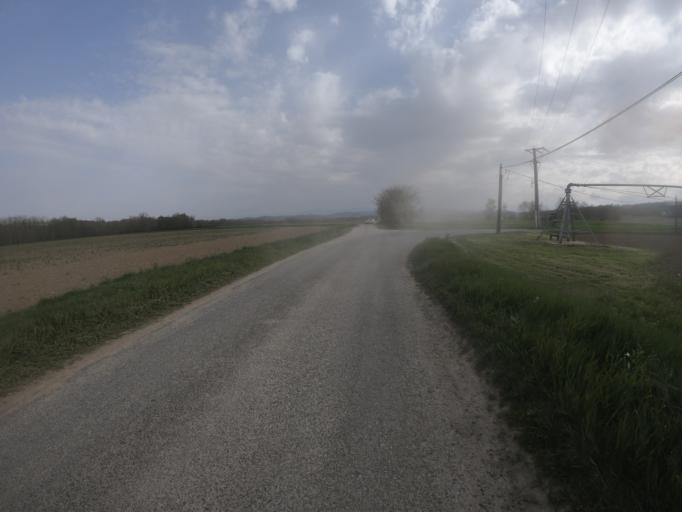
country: FR
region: Midi-Pyrenees
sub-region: Departement de l'Ariege
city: La Tour-du-Crieu
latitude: 43.1214
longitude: 1.7274
